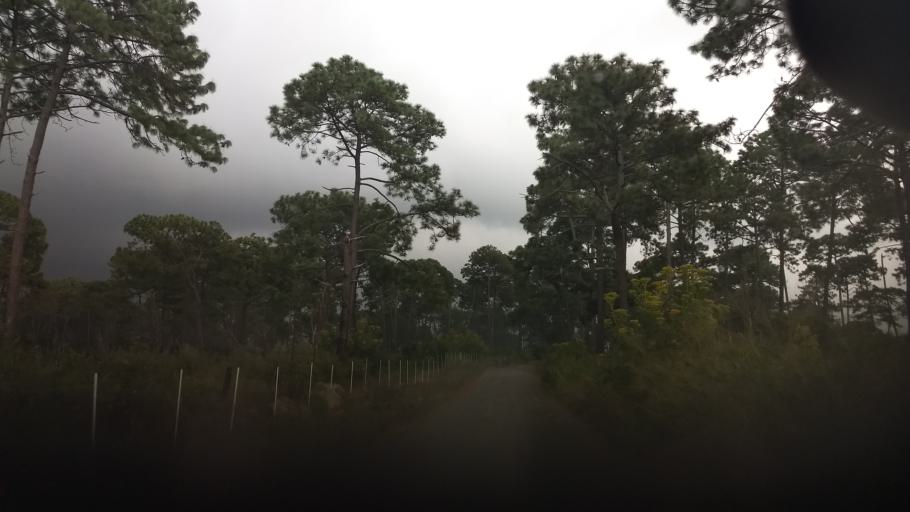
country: MX
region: Jalisco
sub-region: Tonila
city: San Marcos
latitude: 19.4646
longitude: -103.5288
